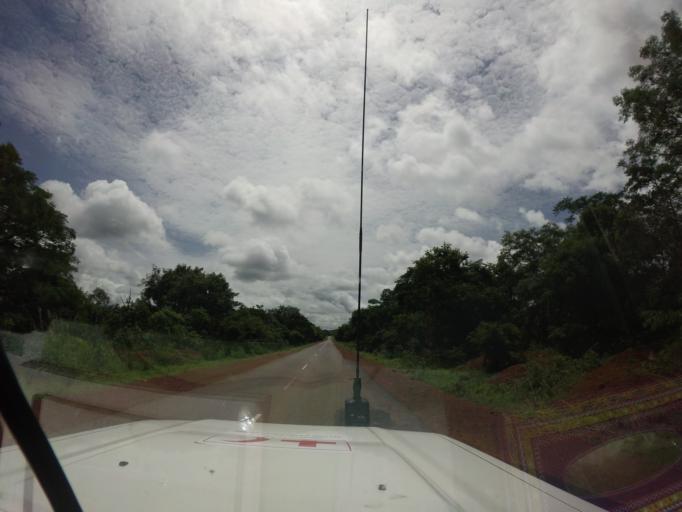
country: SL
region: Northern Province
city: Gberia Fotombu
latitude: 10.1141
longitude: -11.1561
